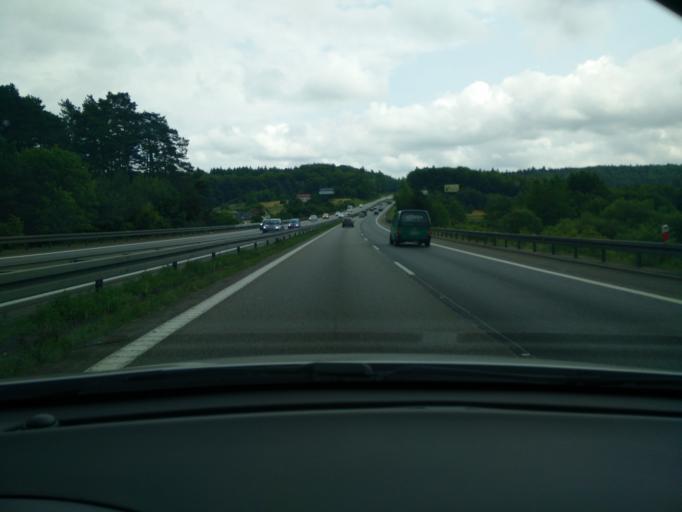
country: PL
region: Pomeranian Voivodeship
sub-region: Gdynia
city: Wielki Kack
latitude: 54.4608
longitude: 18.4871
